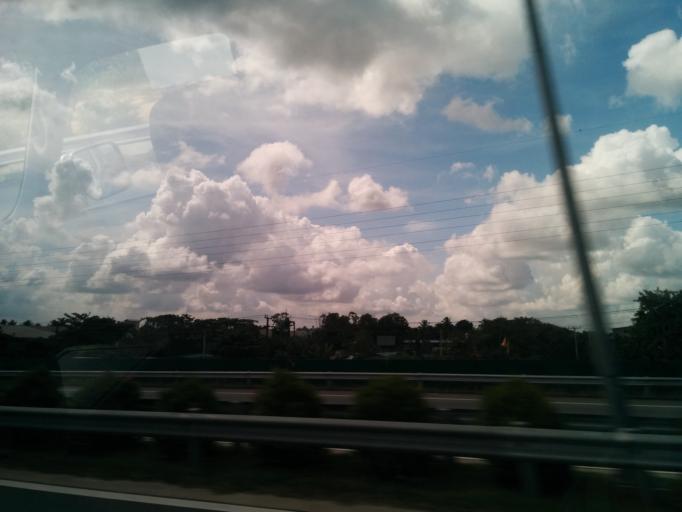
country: LK
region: Western
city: Peliyagoda
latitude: 6.9612
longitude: 79.8876
